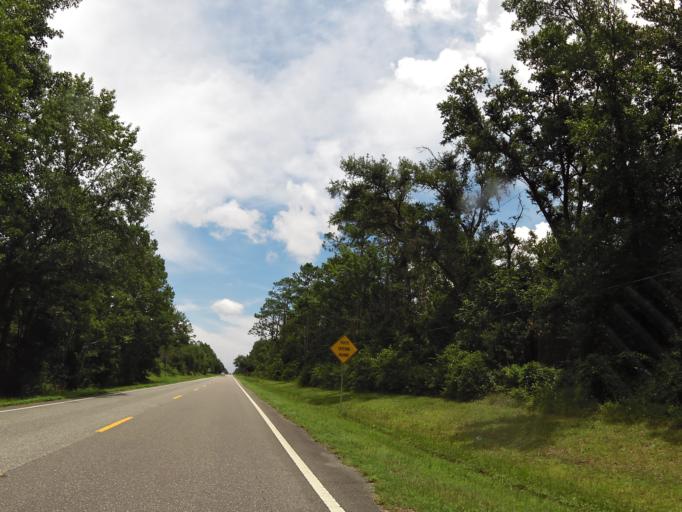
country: US
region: Florida
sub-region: Flagler County
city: Palm Coast
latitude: 29.6560
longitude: -81.3273
